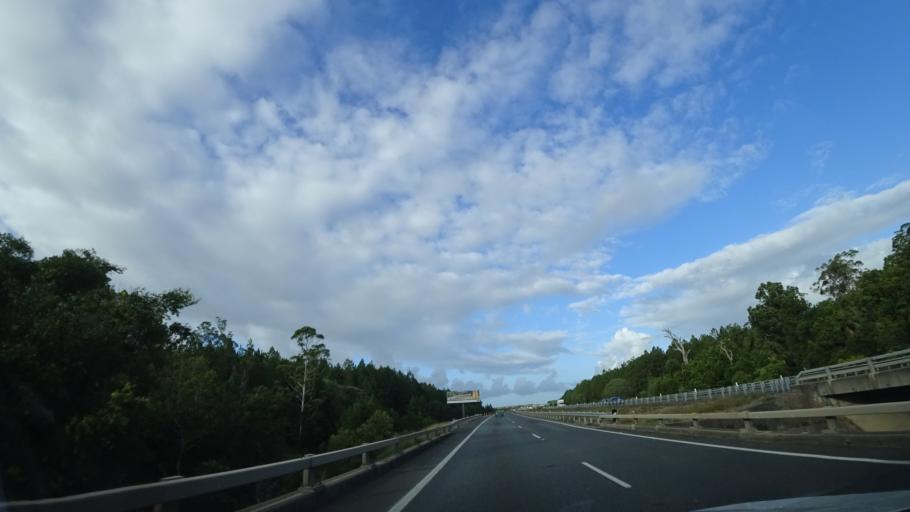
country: AU
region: Queensland
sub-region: Sunshine Coast
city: Little Mountain
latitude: -26.8616
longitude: 153.0161
